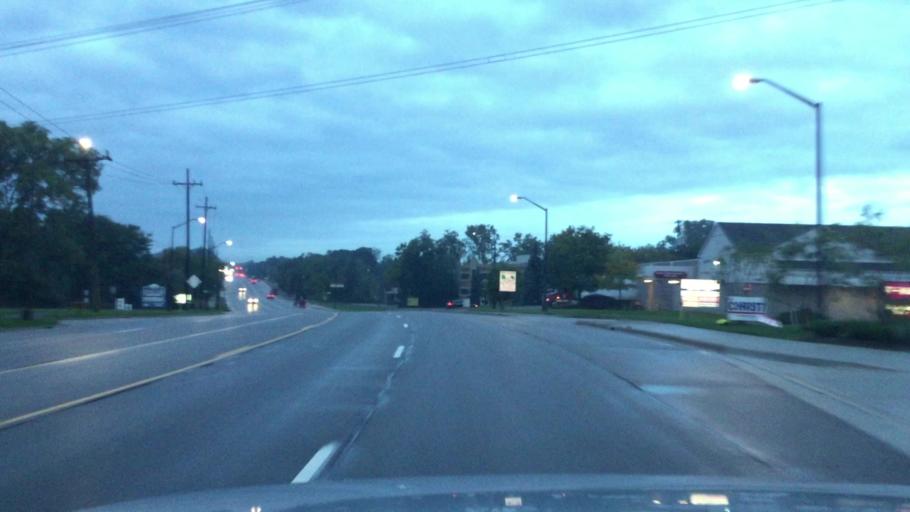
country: US
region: Michigan
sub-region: Oakland County
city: Clarkston
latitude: 42.7212
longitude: -83.4194
